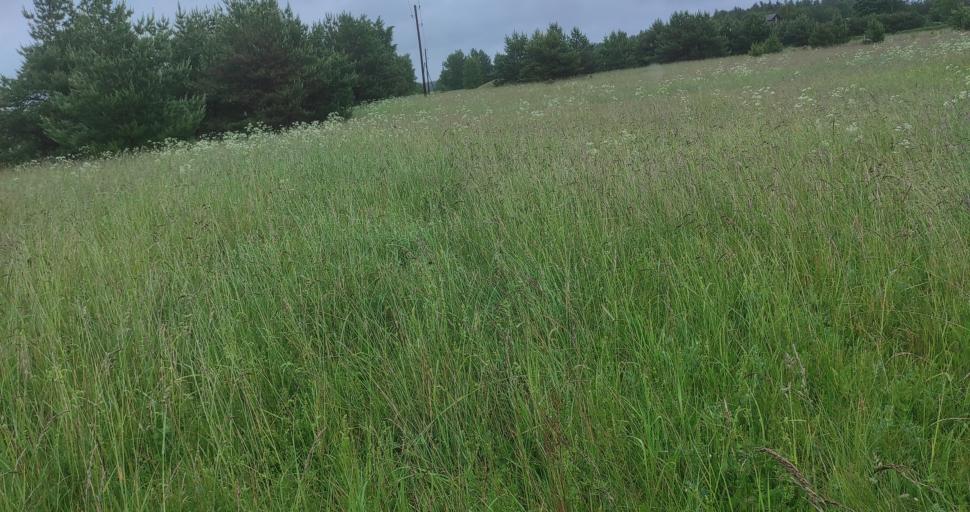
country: LV
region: Pavilostas
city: Pavilosta
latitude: 56.9571
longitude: 21.3167
